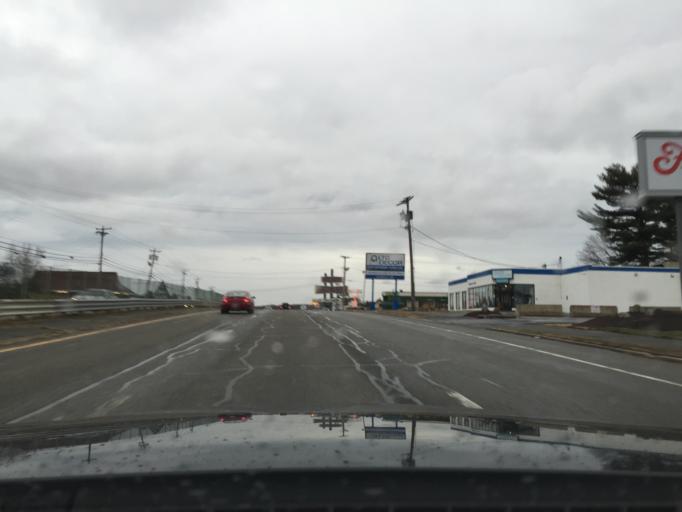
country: US
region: Massachusetts
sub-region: Essex County
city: Saugus
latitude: 42.4767
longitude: -71.0235
